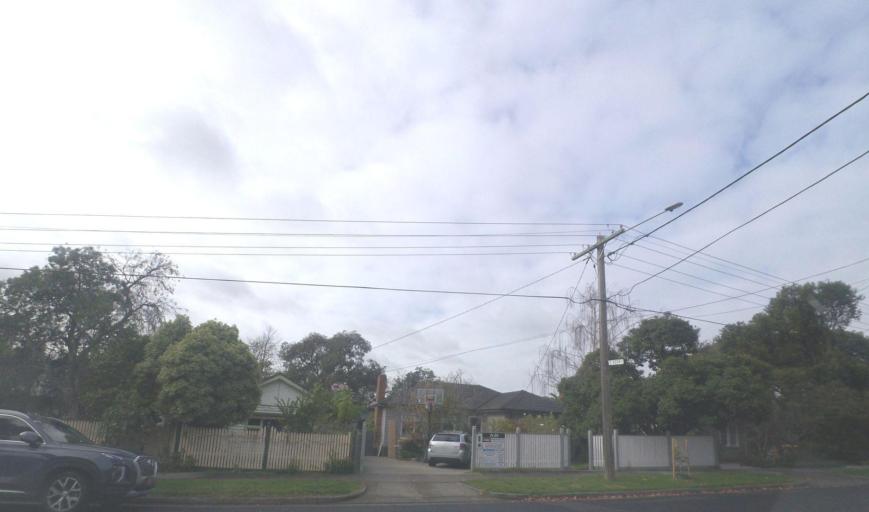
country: AU
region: Victoria
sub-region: Whitehorse
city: Nunawading
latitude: -37.8090
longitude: 145.1740
